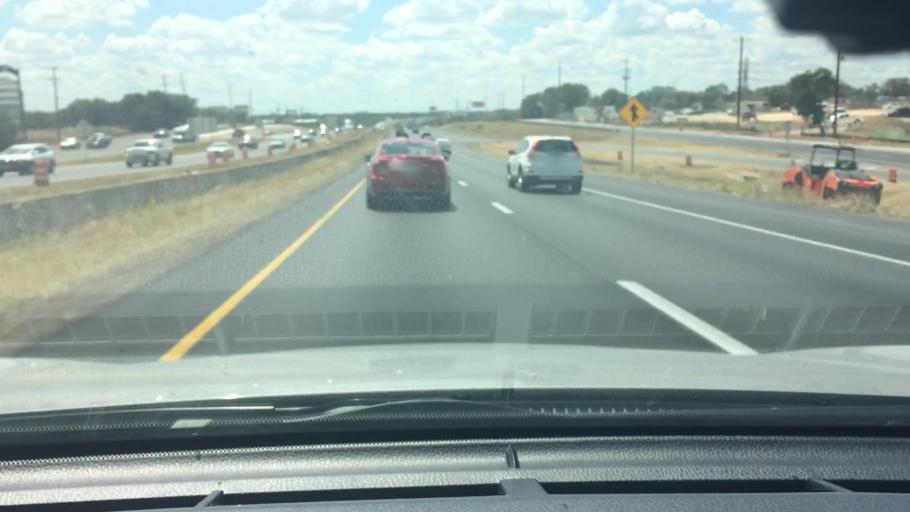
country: US
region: Texas
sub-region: Bexar County
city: Shavano Park
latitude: 29.5992
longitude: -98.5660
